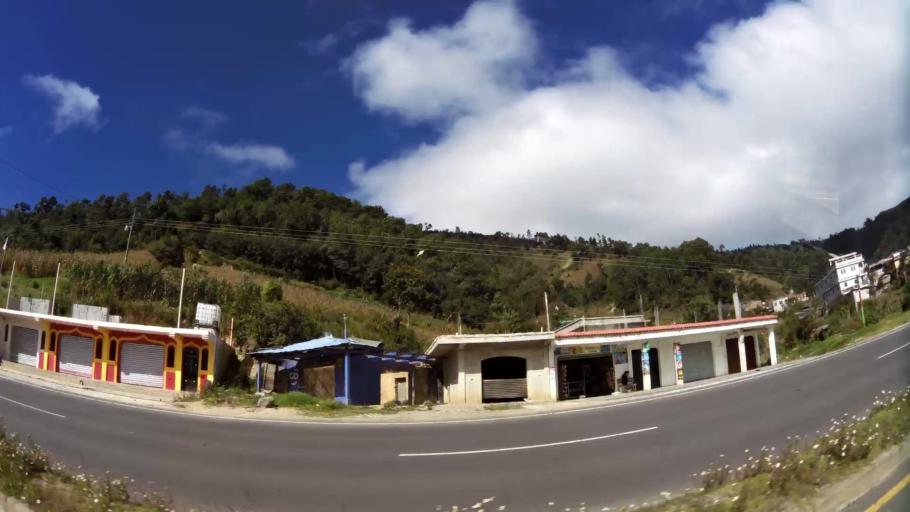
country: GT
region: Solola
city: Concepcion
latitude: 14.8418
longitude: -91.1767
